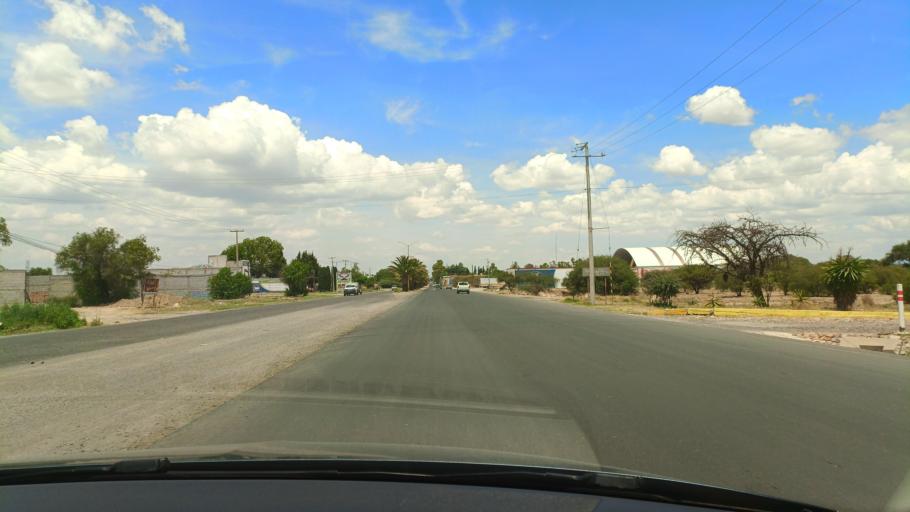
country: MX
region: Guanajuato
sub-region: San Luis de la Paz
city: San Ignacio
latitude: 21.2922
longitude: -100.5414
